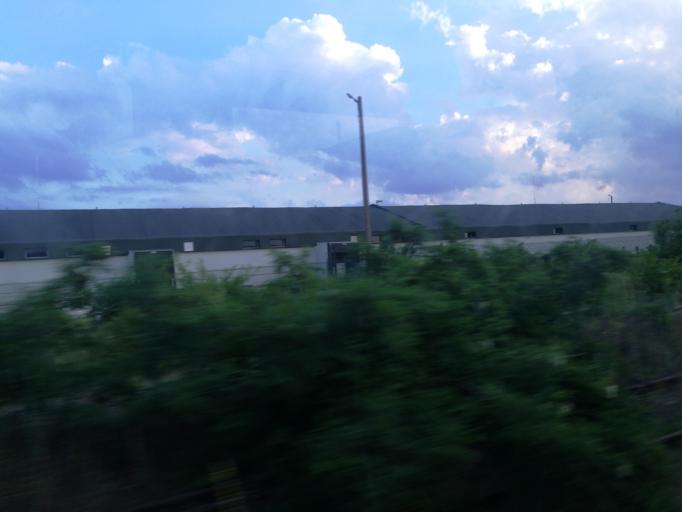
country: RO
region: Dambovita
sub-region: Comuna Produlesti
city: Costestii din Deal
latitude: 44.6741
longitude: 25.5012
